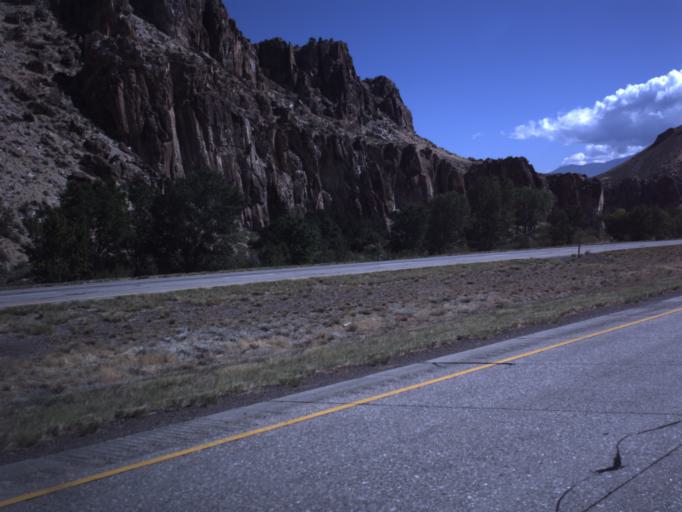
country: US
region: Utah
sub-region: Sevier County
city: Monroe
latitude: 38.5790
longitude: -112.2865
